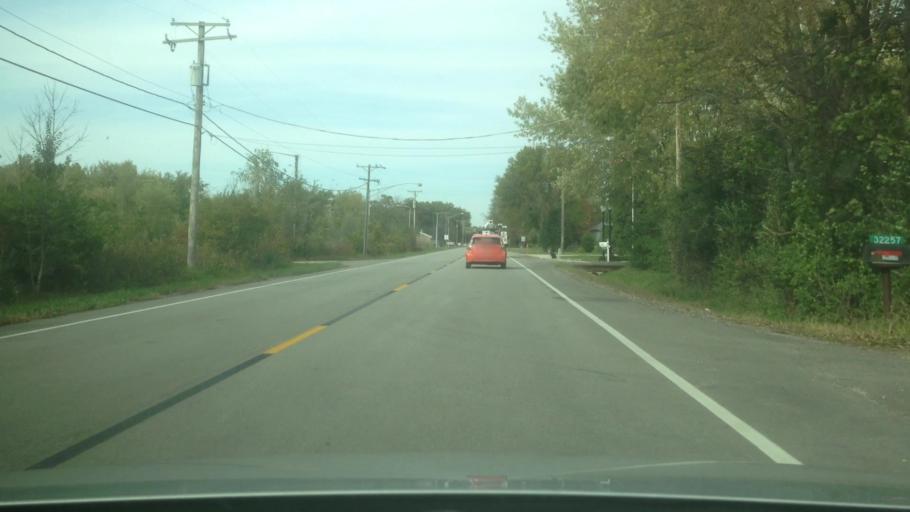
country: US
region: Illinois
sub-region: Will County
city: Wilmington
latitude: 41.2979
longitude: -88.1586
